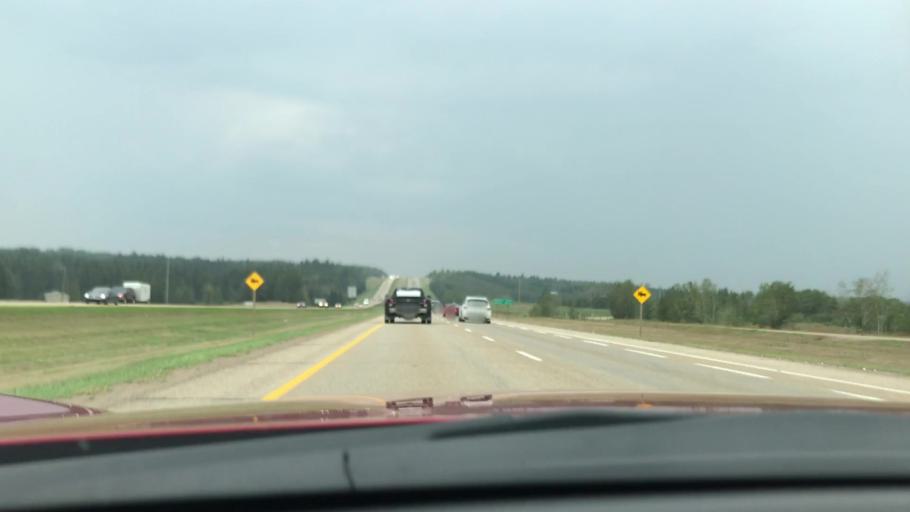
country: CA
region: Alberta
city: Blackfalds
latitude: 52.3629
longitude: -113.8313
